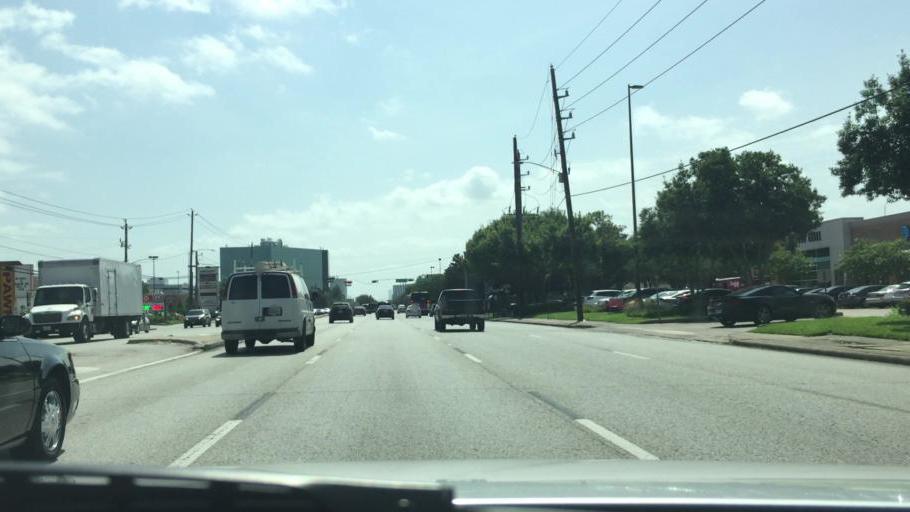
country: US
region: Texas
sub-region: Harris County
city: Bunker Hill Village
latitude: 29.7365
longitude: -95.5866
